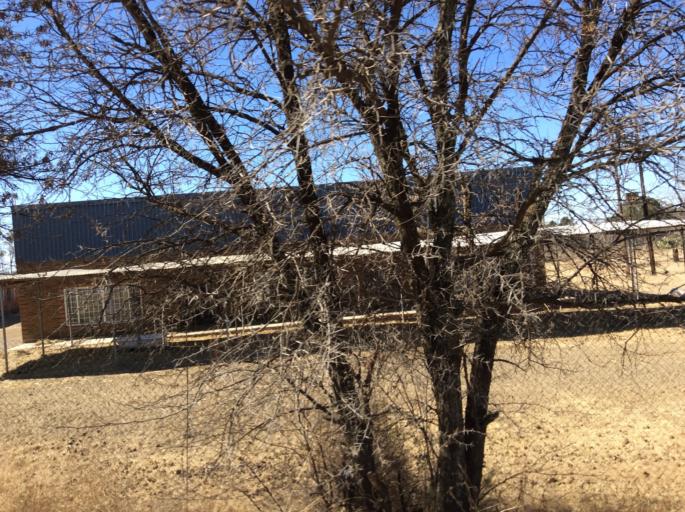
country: ZA
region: Orange Free State
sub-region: Lejweleputswa District Municipality
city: Brandfort
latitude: -28.7209
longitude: 26.0650
